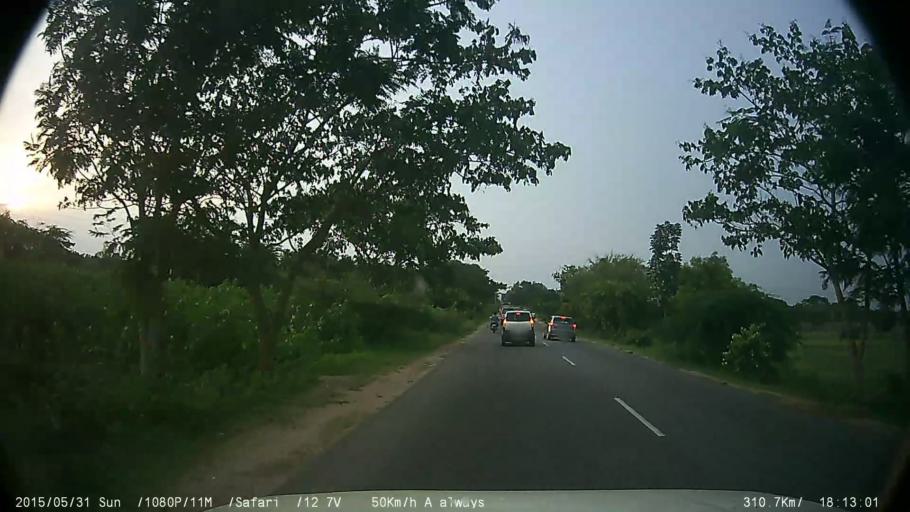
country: IN
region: Karnataka
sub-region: Mysore
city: Nanjangud
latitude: 12.0998
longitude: 76.6719
